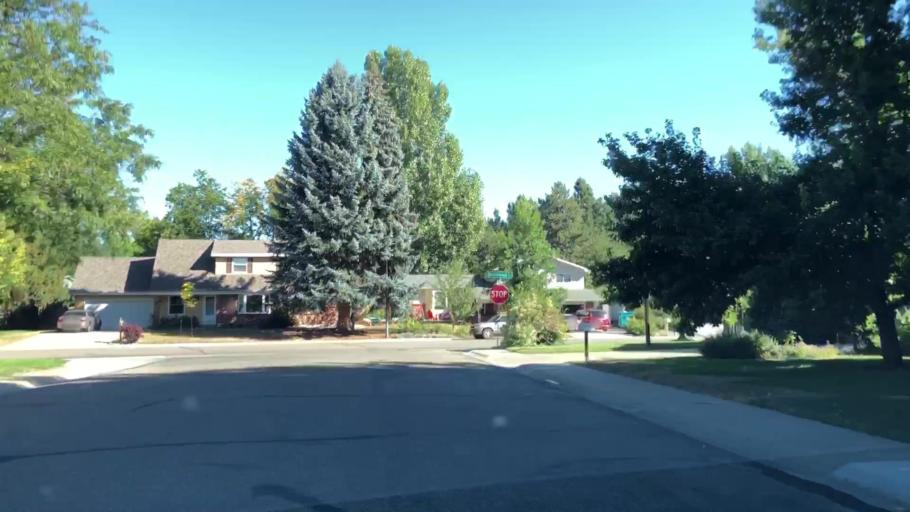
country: US
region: Colorado
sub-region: Larimer County
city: Fort Collins
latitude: 40.5575
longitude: -105.0509
